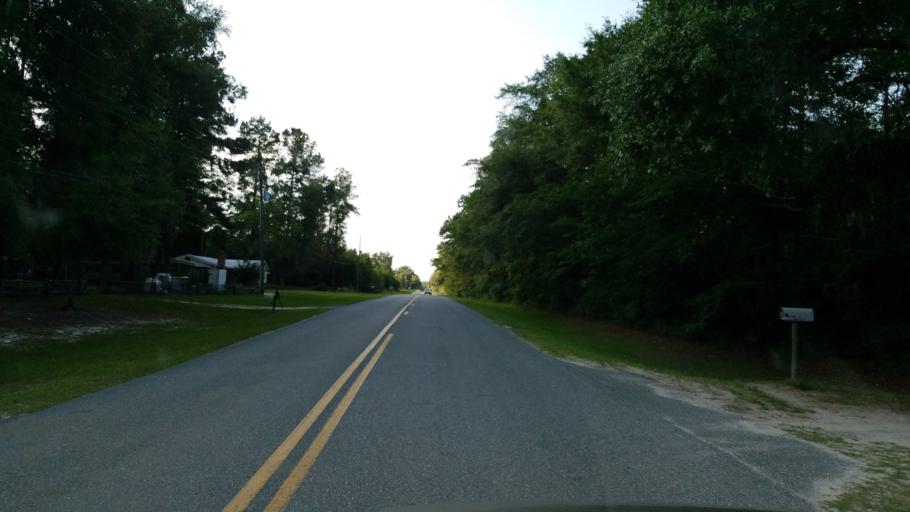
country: US
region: Georgia
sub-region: Echols County
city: Statenville
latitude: 30.6076
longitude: -83.0947
